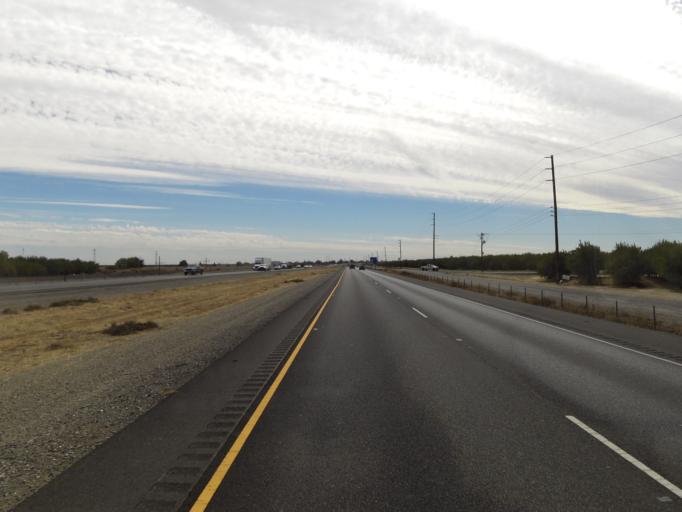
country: US
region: California
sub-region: Colusa County
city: Arbuckle
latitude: 39.0365
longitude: -122.0700
